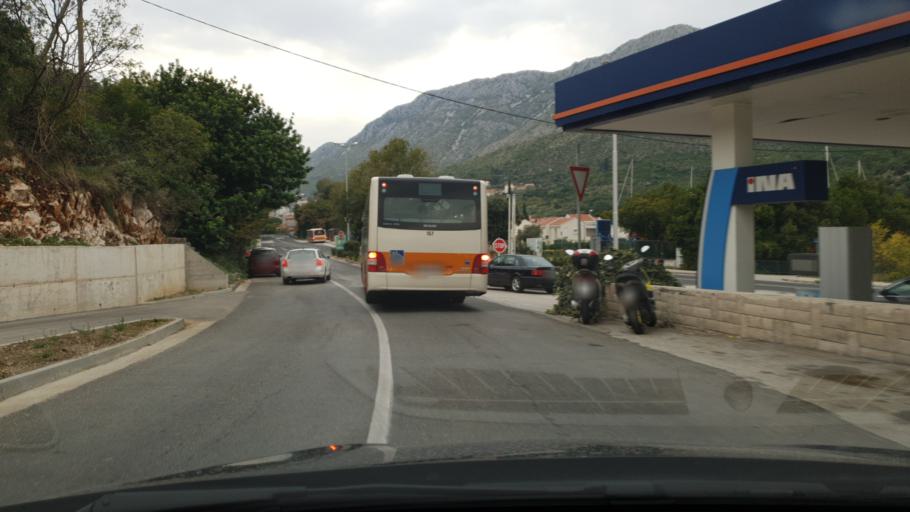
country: HR
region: Dubrovacko-Neretvanska
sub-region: Grad Dubrovnik
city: Mokosica
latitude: 42.6682
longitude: 18.1297
